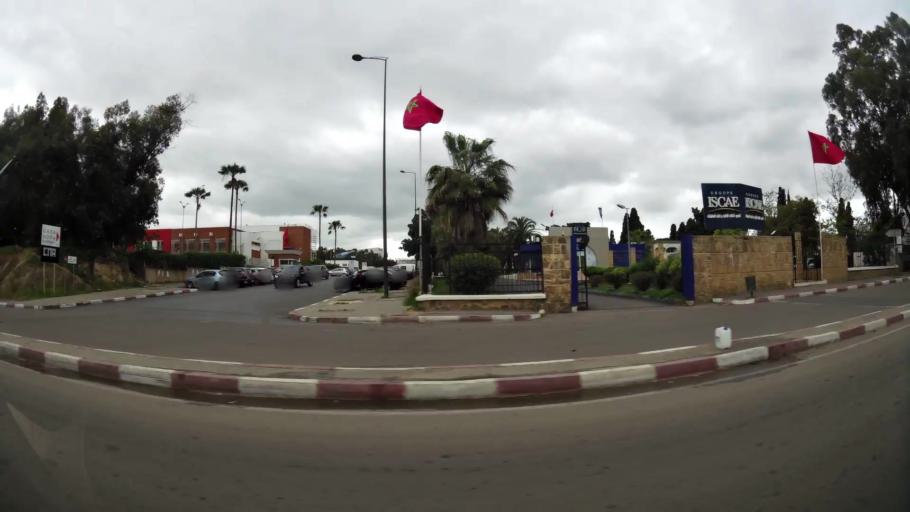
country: MA
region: Grand Casablanca
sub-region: Casablanca
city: Casablanca
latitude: 33.5268
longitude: -7.6361
